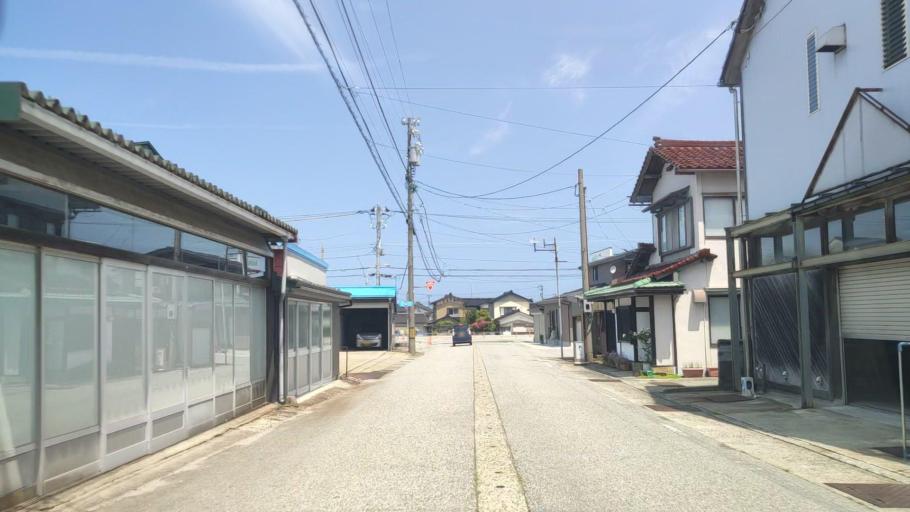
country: JP
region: Toyama
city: Nyuzen
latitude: 36.9578
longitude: 137.5592
